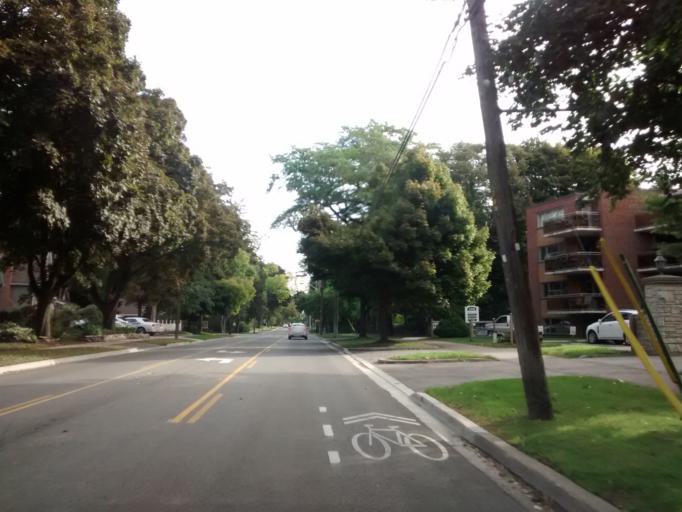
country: CA
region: Ontario
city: Burlington
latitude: 43.3308
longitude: -79.7831
